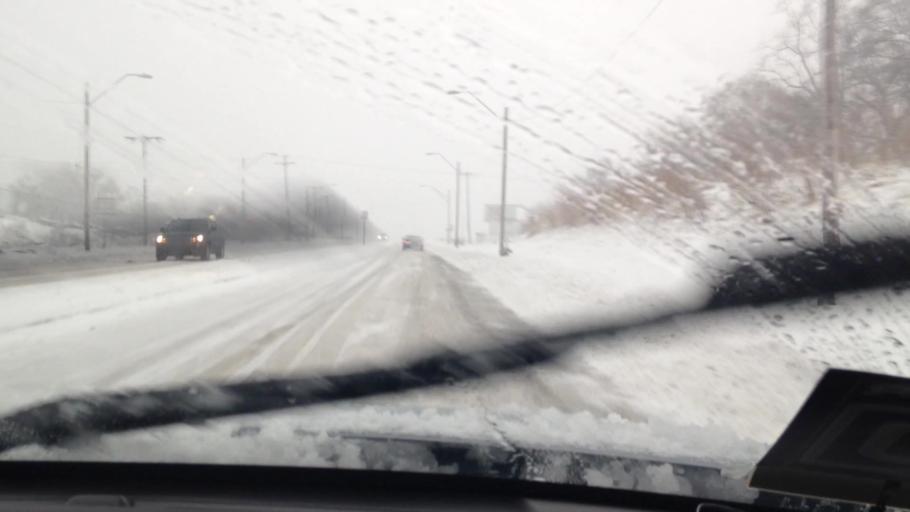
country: US
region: Missouri
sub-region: Jackson County
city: Sugar Creek
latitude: 39.0680
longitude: -94.4992
